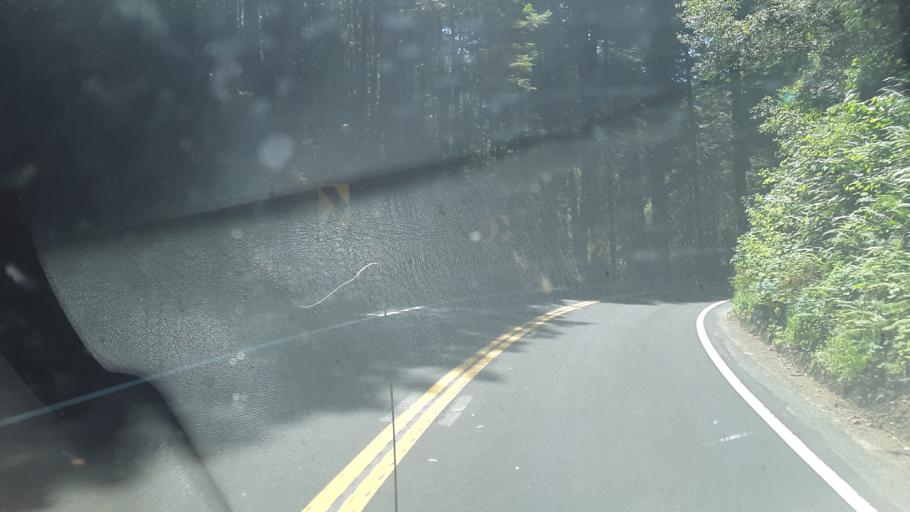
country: US
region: California
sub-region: Del Norte County
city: Bertsch-Oceanview
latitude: 41.8301
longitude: -124.0324
